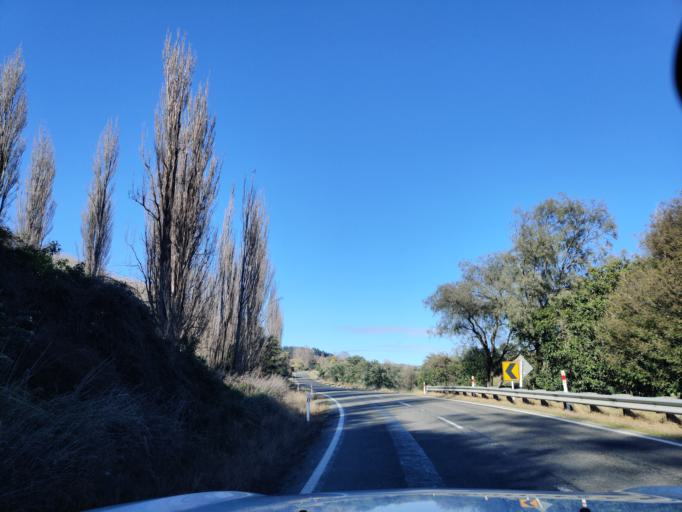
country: NZ
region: Manawatu-Wanganui
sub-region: Rangitikei District
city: Bulls
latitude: -39.9653
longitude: 175.6394
